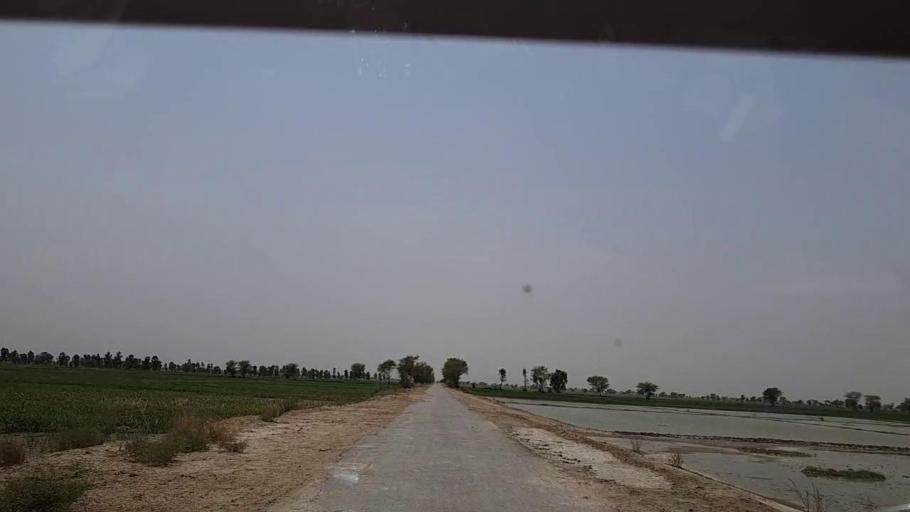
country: PK
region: Sindh
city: Khairpur Nathan Shah
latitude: 27.0060
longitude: 67.6512
